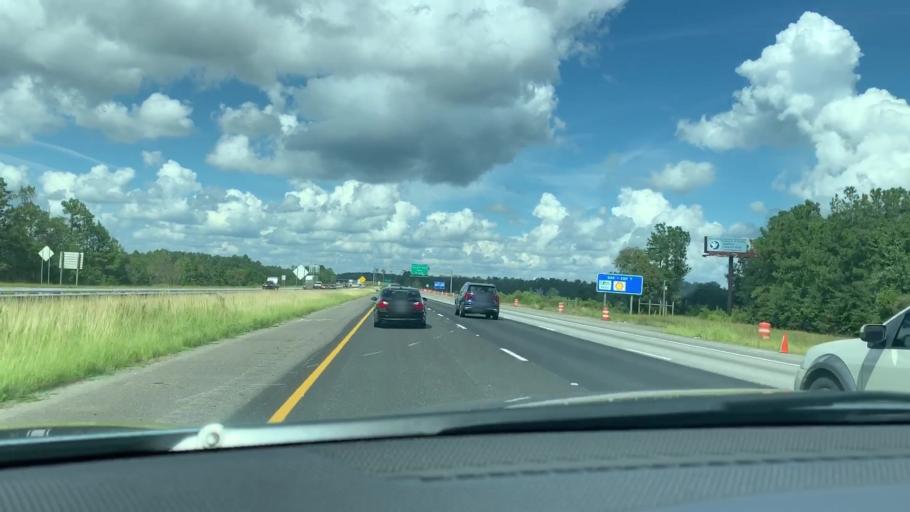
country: US
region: Georgia
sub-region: Camden County
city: Kingsland
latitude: 30.8344
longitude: -81.6684
